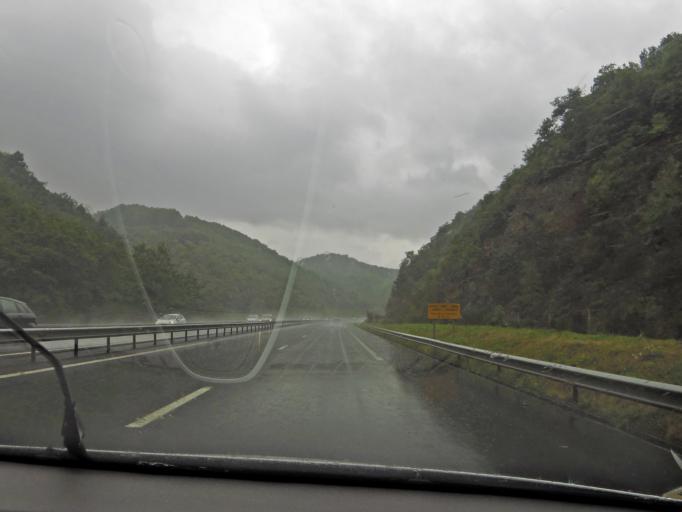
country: FR
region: Auvergne
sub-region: Departement du Cantal
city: Massiac
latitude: 45.2035
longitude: 3.1960
